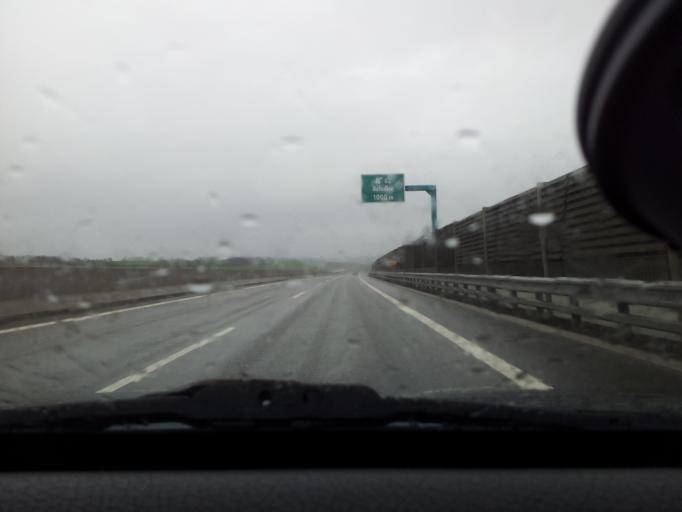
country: SK
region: Nitriansky
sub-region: Okres Nitra
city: Vrable
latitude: 48.3309
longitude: 18.2863
